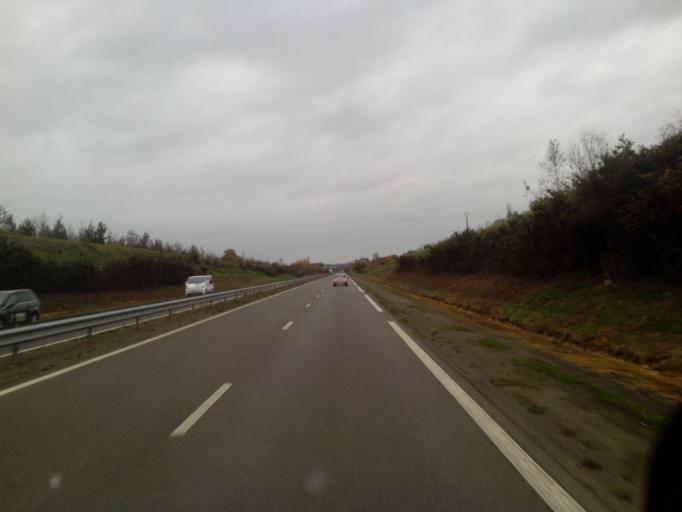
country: FR
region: Brittany
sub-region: Departement d'Ille-et-Vilaine
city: Betton
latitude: 48.1694
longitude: -1.6263
